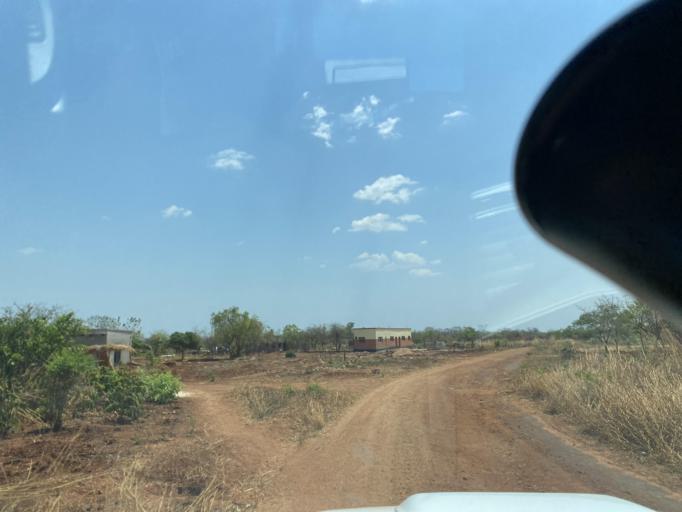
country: ZM
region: Lusaka
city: Lusaka
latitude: -15.5065
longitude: 28.0196
